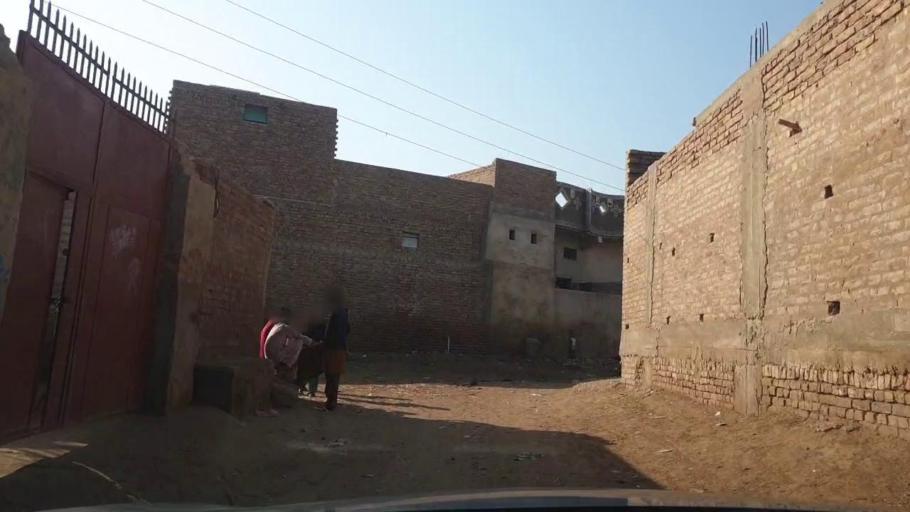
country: PK
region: Sindh
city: Tando Allahyar
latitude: 25.4922
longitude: 68.7326
